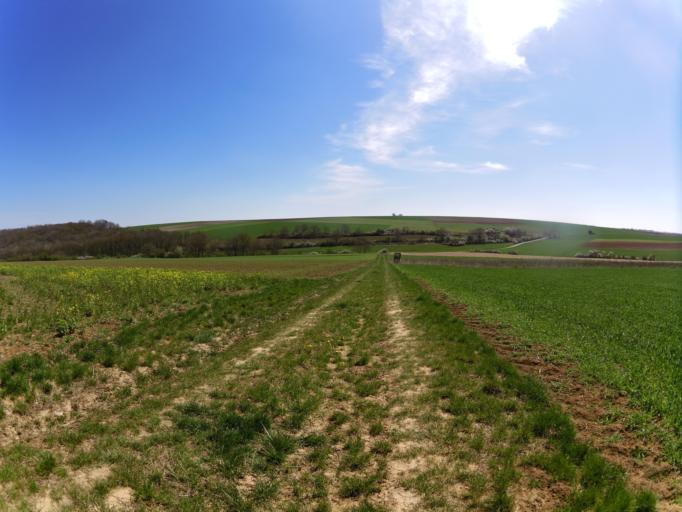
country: DE
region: Bavaria
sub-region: Regierungsbezirk Unterfranken
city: Winterhausen
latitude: 49.6945
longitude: 9.9929
